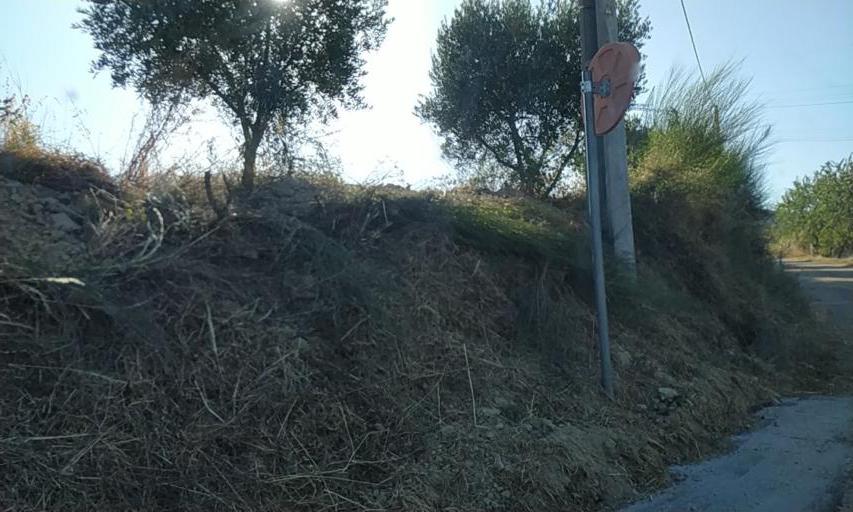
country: PT
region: Viseu
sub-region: Sao Joao da Pesqueira
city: Sao Joao da Pesqueira
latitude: 41.1543
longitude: -7.4207
